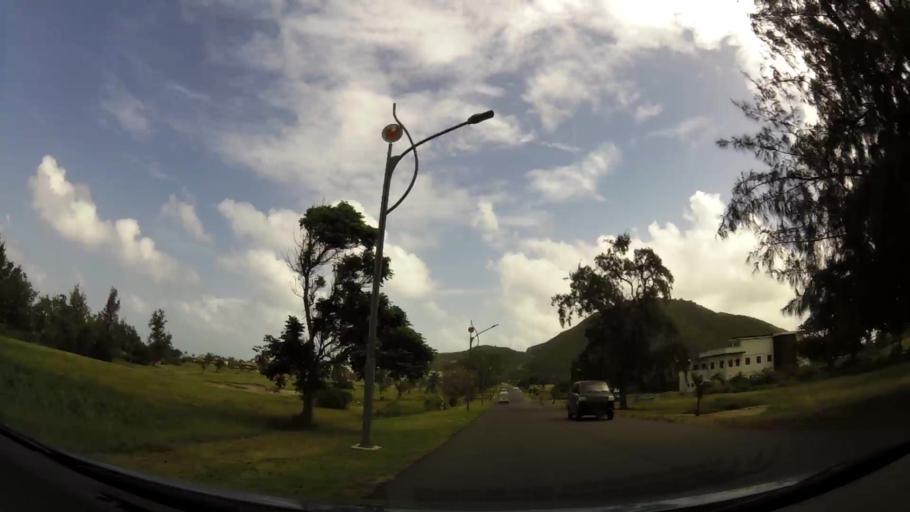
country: KN
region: Saint George Basseterre
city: Basseterre
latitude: 17.2854
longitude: -62.6900
